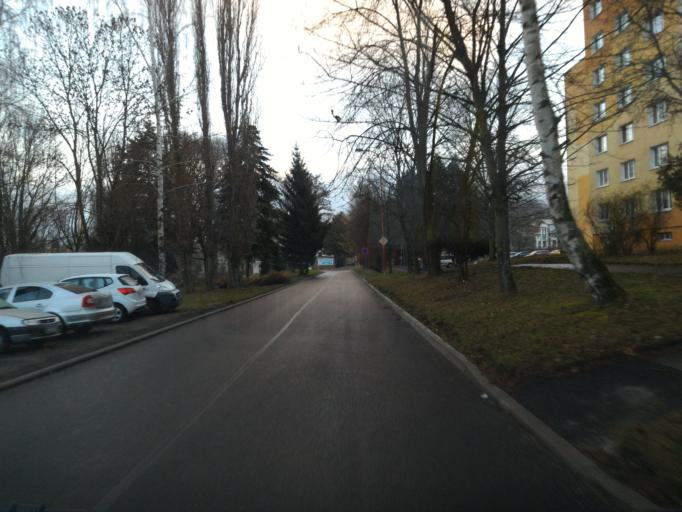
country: CZ
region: Ustecky
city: Varnsdorf
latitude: 50.9058
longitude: 14.6266
